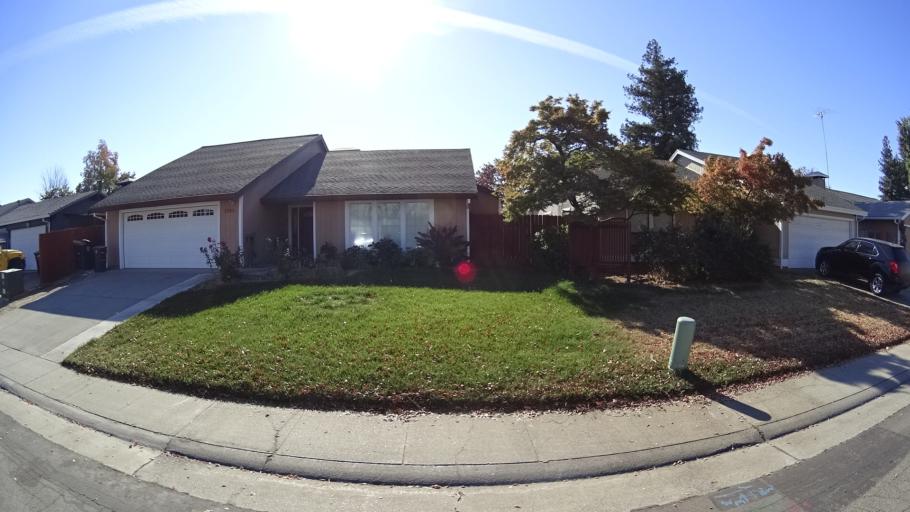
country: US
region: California
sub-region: Sacramento County
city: Antelope
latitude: 38.7199
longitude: -121.3071
